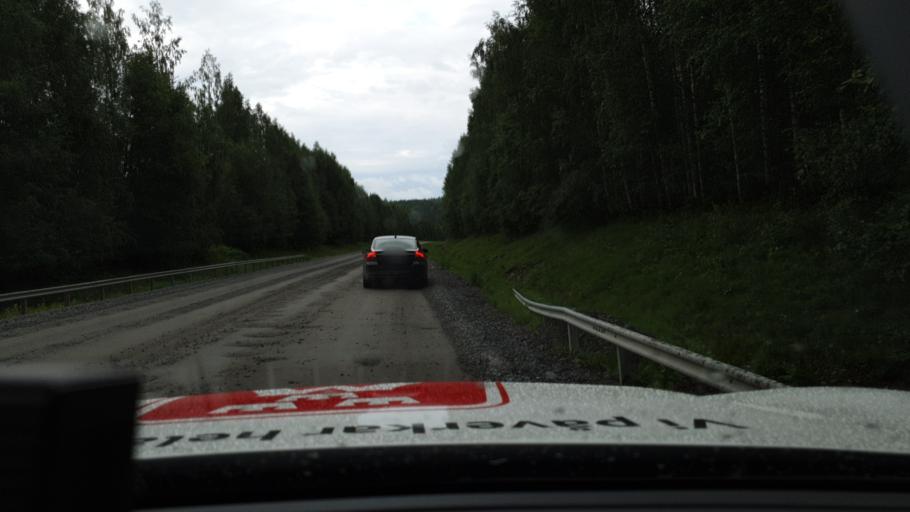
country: SE
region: Norrbotten
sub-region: Bodens Kommun
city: Boden
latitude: 65.8495
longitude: 21.5830
